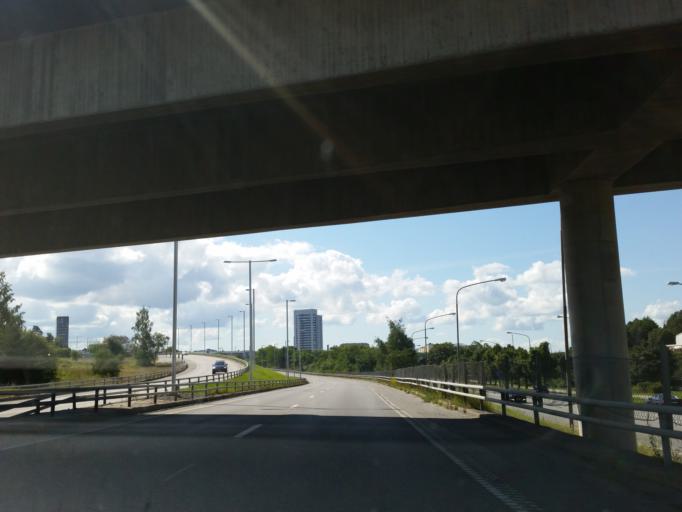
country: SE
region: Stockholm
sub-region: Solna Kommun
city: Solna
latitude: 59.3474
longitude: 18.0099
